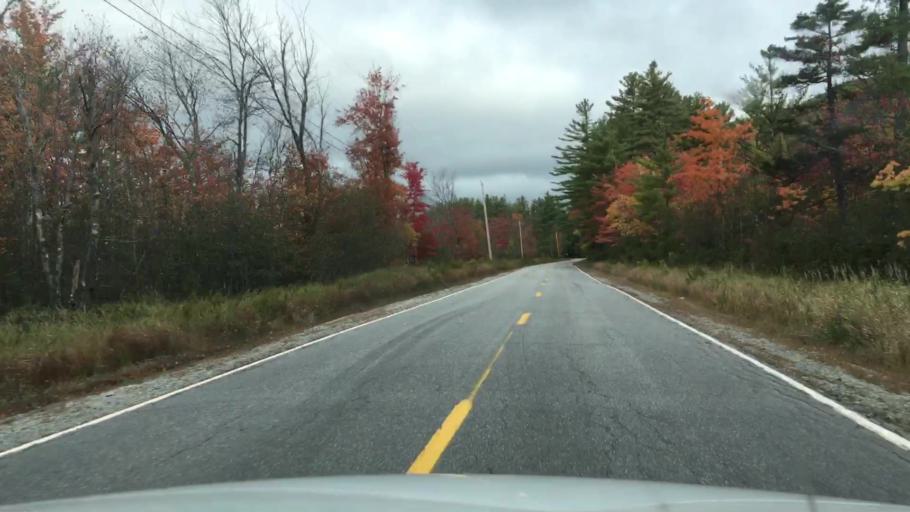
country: US
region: Maine
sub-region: Oxford County
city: Bethel
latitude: 44.3280
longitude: -70.7723
